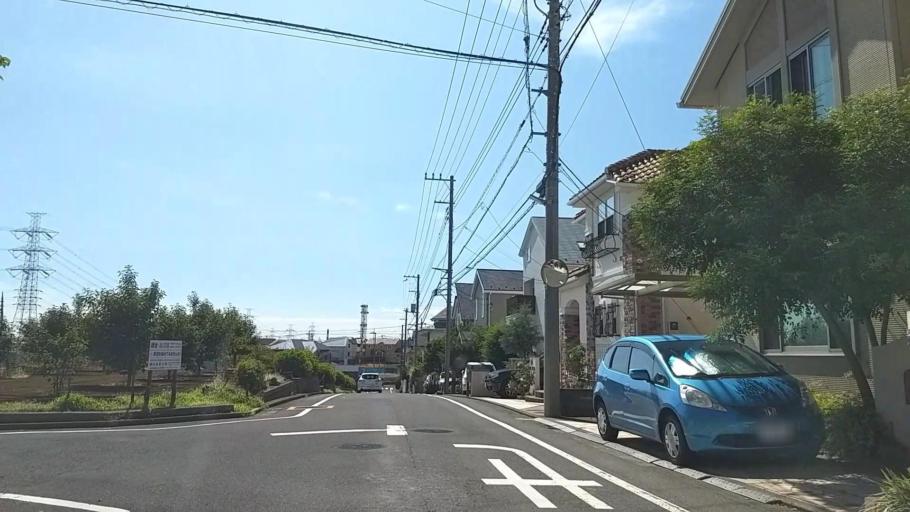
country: JP
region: Tokyo
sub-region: Machida-shi
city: Machida
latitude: 35.5624
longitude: 139.5418
